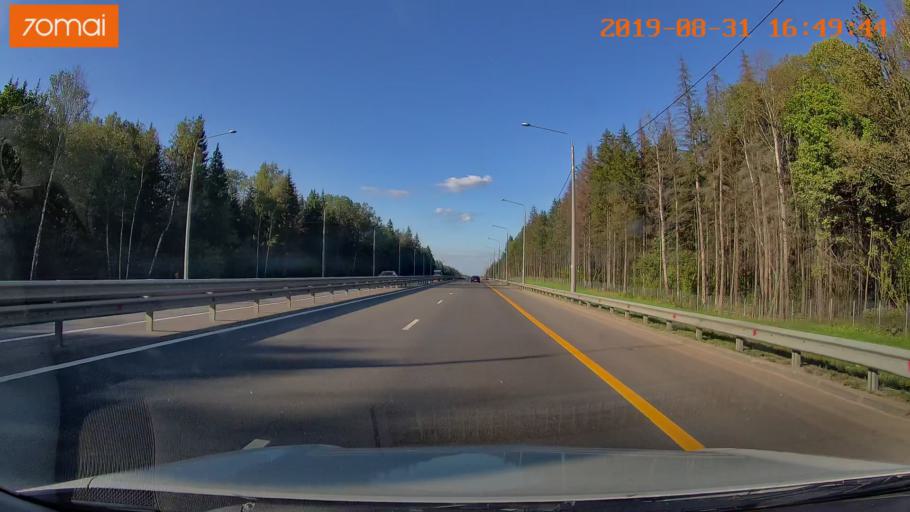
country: RU
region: Kaluga
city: Pyatovskiy
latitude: 54.6959
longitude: 36.1571
